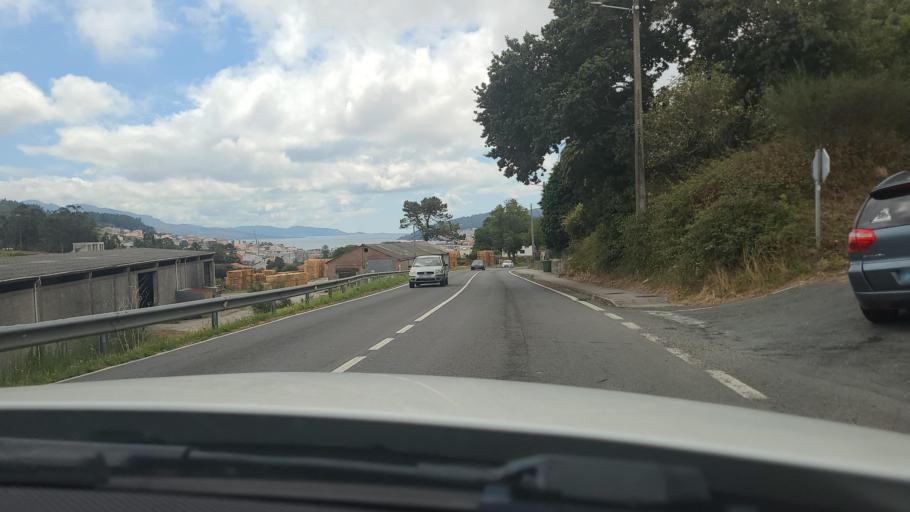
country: ES
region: Galicia
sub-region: Provincia da Coruna
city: Cee
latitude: 42.9648
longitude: -9.1936
